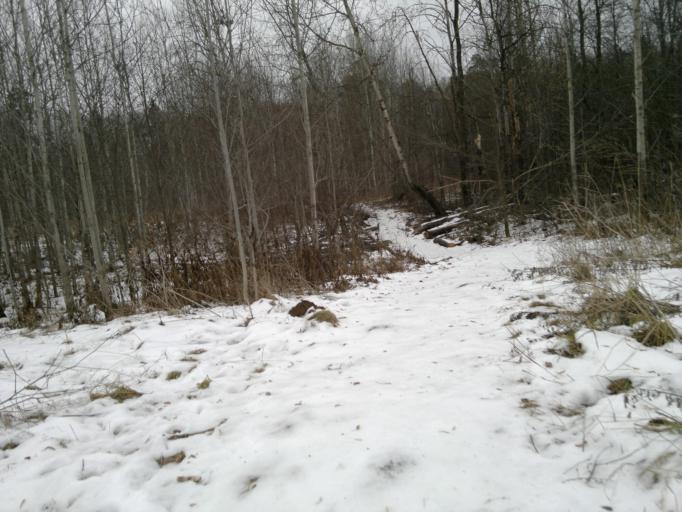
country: RU
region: Mariy-El
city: Yoshkar-Ola
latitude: 56.6124
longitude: 47.9335
